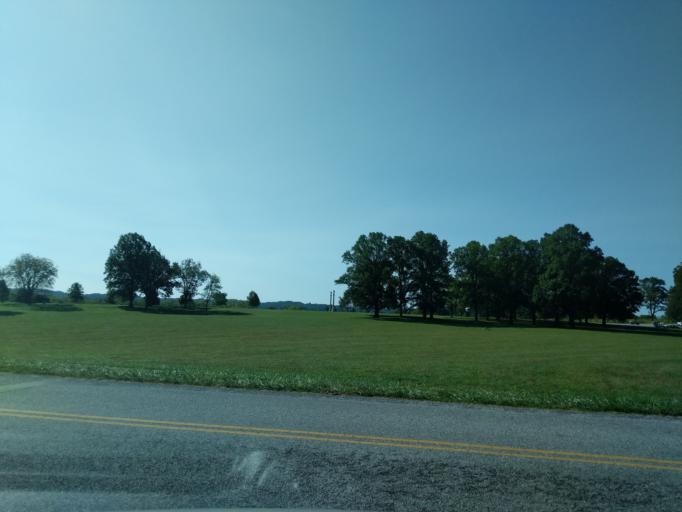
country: US
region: Pennsylvania
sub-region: Chester County
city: Chesterbrook
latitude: 40.0910
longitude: -75.4388
